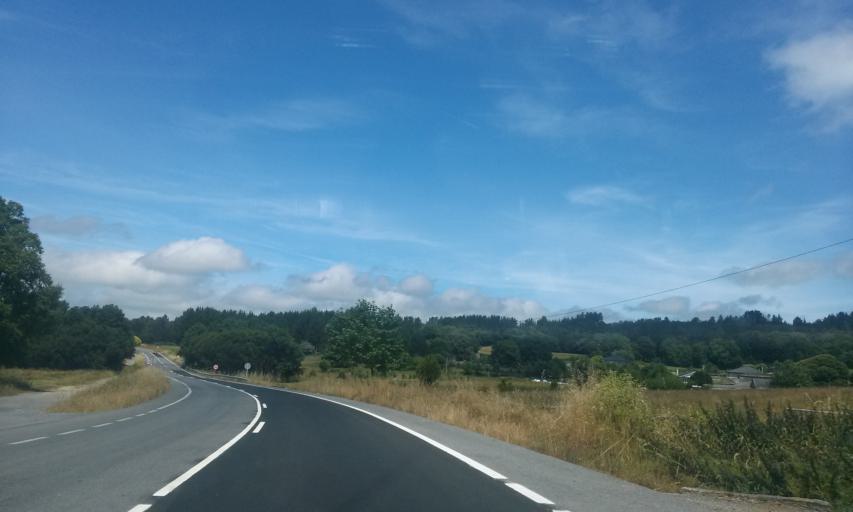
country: ES
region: Galicia
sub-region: Provincia de Lugo
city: Lugo
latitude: 43.0111
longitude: -7.6515
